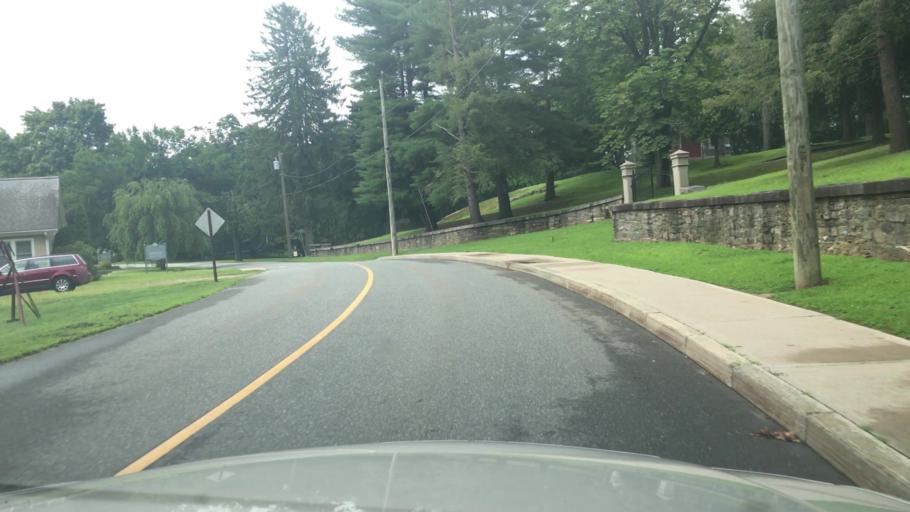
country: US
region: Connecticut
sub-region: Middlesex County
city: Deep River Center
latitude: 41.3855
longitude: -72.4323
